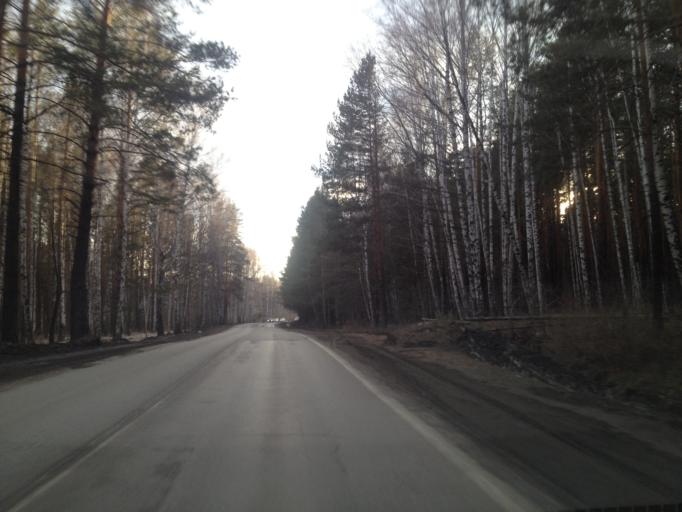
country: RU
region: Sverdlovsk
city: Shirokaya Rechka
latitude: 56.8152
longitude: 60.4514
